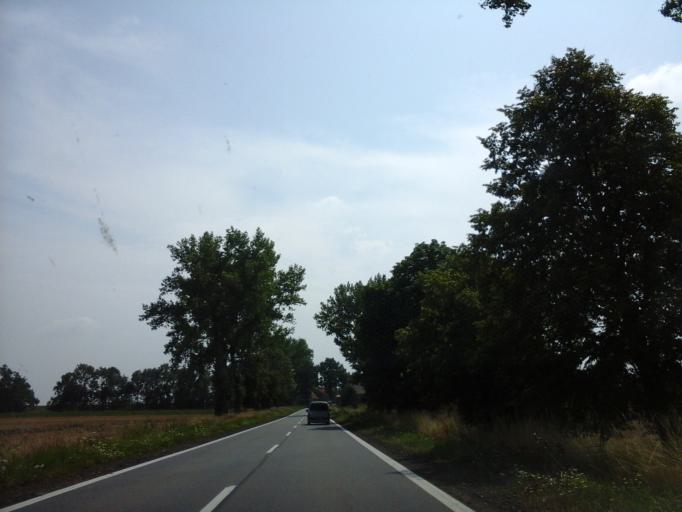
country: PL
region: Lower Silesian Voivodeship
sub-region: Powiat wroclawski
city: Zorawina
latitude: 50.9984
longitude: 17.0669
